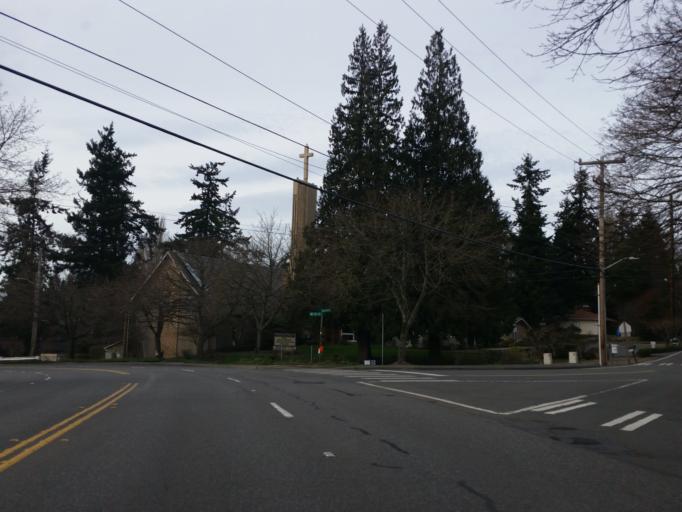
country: US
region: Washington
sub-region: Snohomish County
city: Woodway
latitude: 47.7703
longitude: -122.3772
